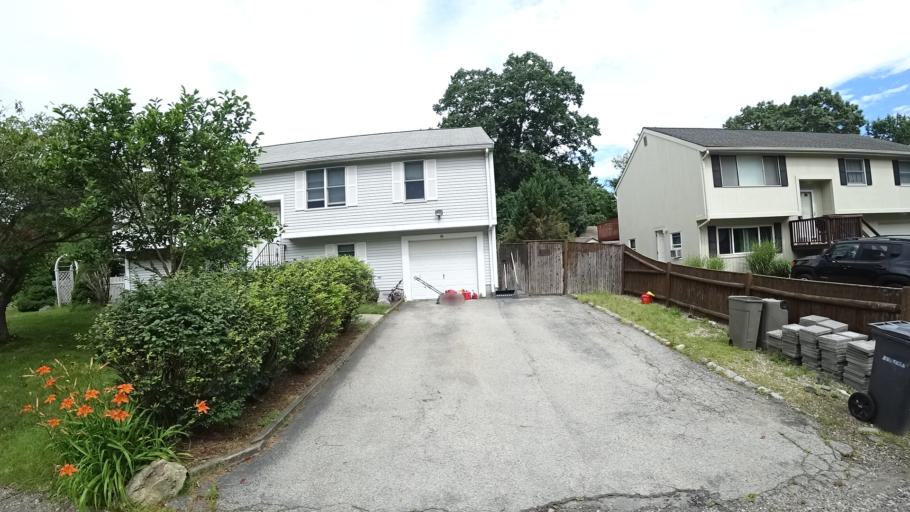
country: US
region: Massachusetts
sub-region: Norfolk County
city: Dedham
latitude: 42.2263
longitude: -71.1455
